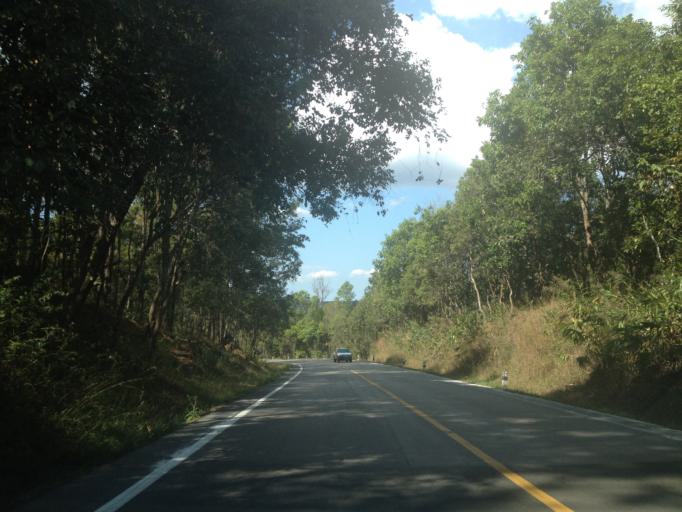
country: TH
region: Mae Hong Son
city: Pa Pae
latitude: 18.1472
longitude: 98.3095
